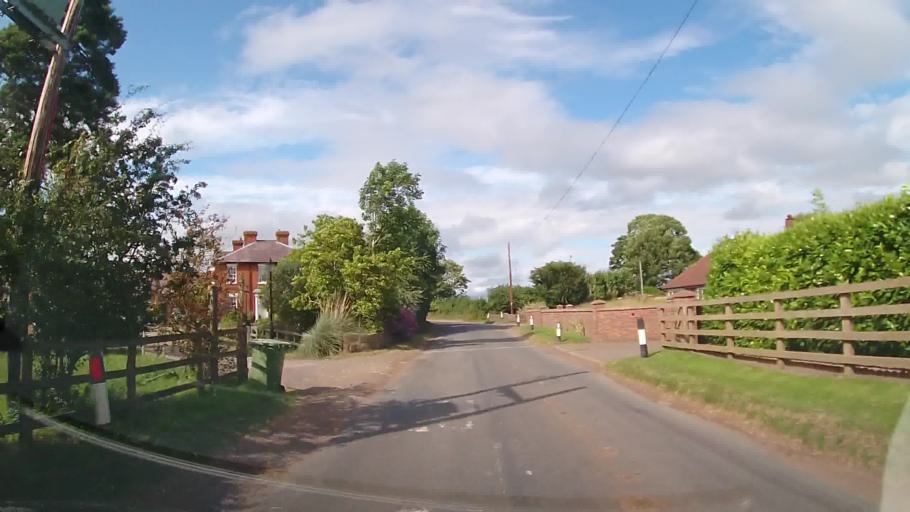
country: GB
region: England
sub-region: Shropshire
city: Petton
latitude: 52.8393
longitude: -2.8053
